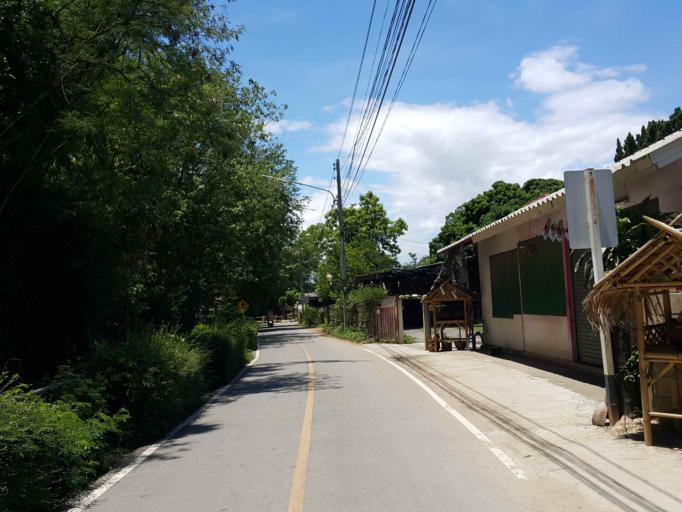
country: TH
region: Chiang Mai
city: Chiang Mai
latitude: 18.7493
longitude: 98.9975
